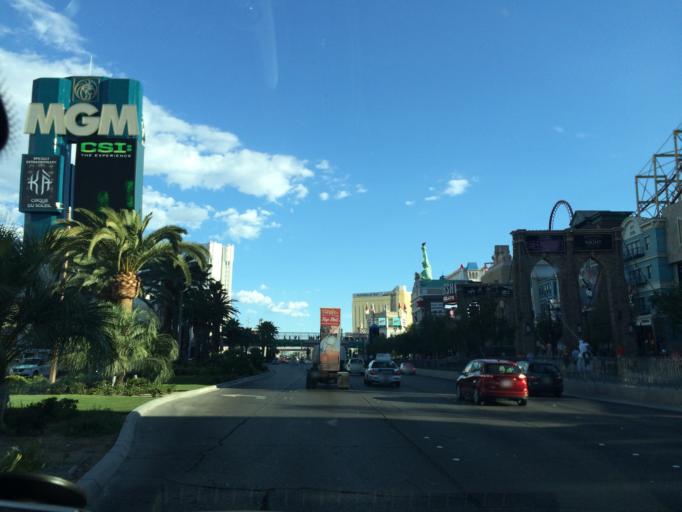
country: US
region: Nevada
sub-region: Clark County
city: Paradise
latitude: 36.1033
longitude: -115.1731
